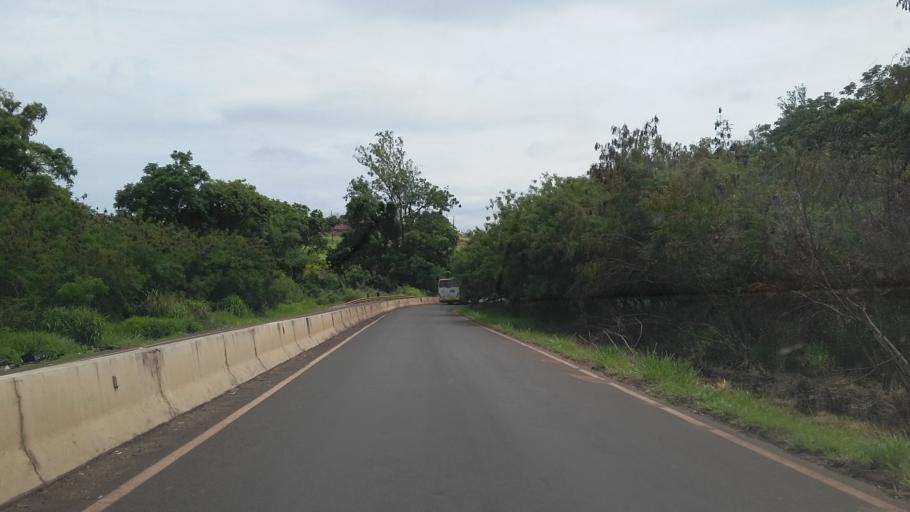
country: BR
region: Parana
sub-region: Londrina
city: Londrina
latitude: -23.2916
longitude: -51.1499
